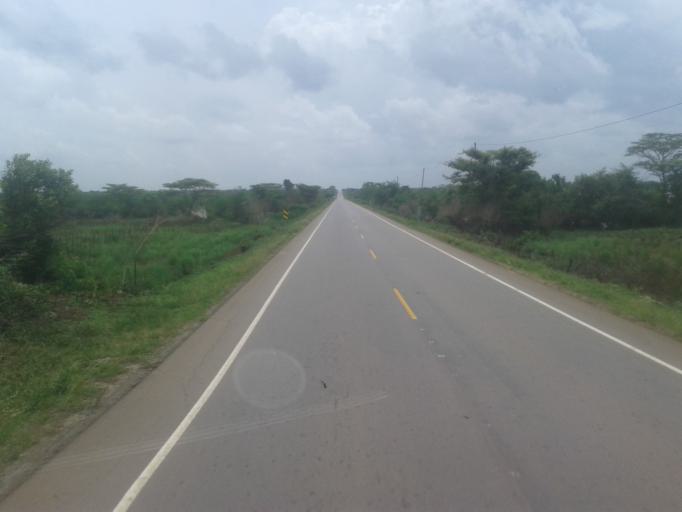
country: UG
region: Western Region
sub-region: Kiryandongo District
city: Masindi Port
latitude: 1.6668
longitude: 32.0305
